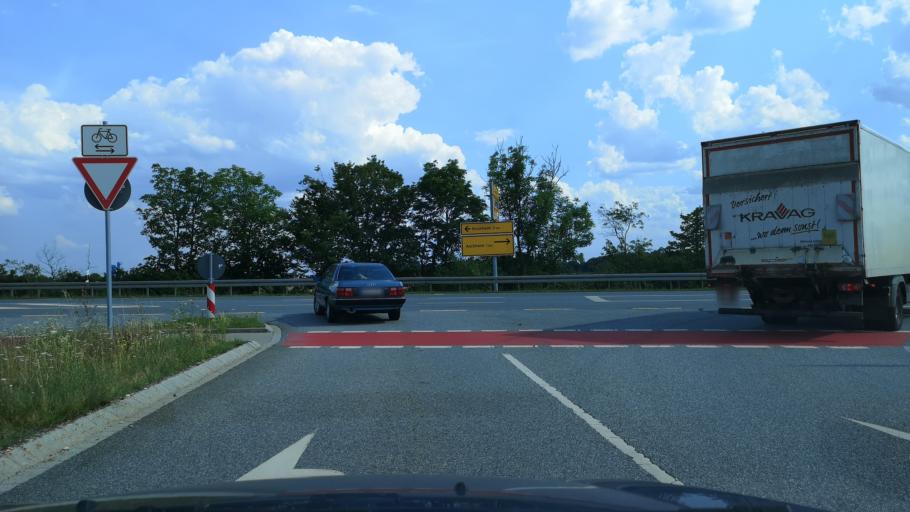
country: DE
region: Bavaria
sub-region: Upper Bavaria
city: Aschheim
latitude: 48.1731
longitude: 11.7310
